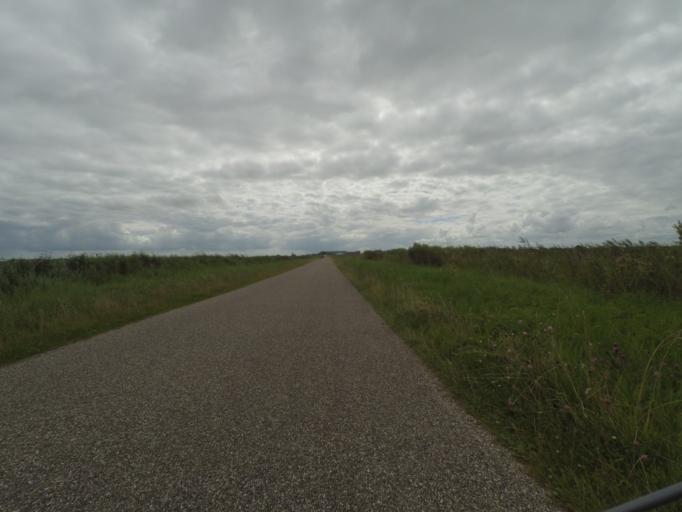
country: NL
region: Friesland
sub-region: Gemeente Dongeradeel
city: Anjum
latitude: 53.3478
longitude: 6.1530
